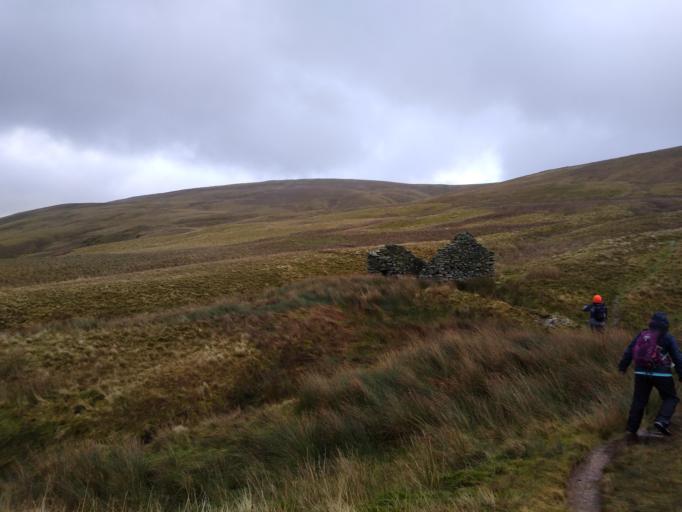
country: GB
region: England
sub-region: Cumbria
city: Ambleside
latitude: 54.5445
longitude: -2.8567
